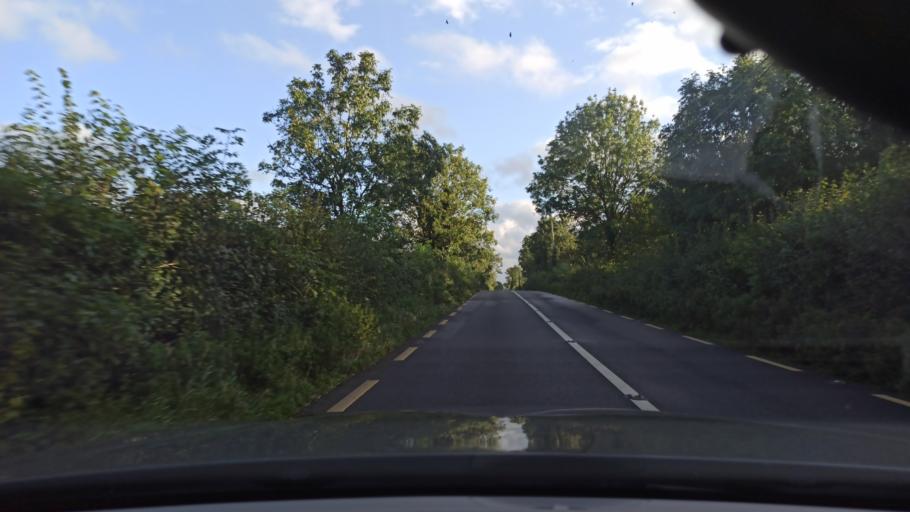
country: IE
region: Munster
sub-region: North Tipperary
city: Roscrea
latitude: 52.8919
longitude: -7.8015
